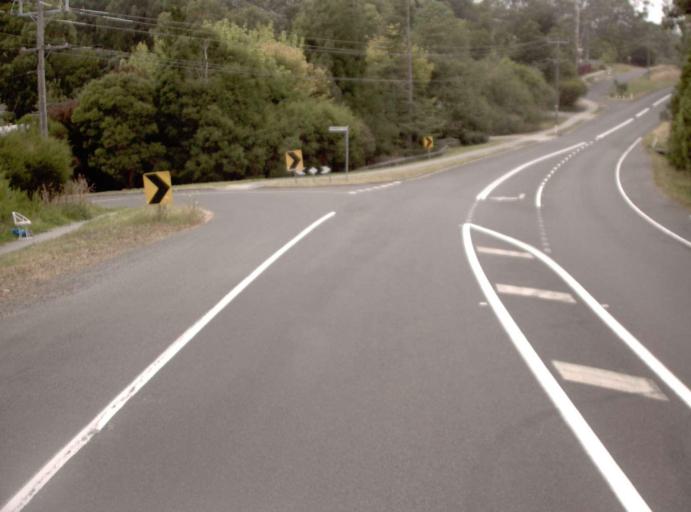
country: AU
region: Victoria
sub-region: Yarra Ranges
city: Healesville
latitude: -37.6751
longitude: 145.5327
